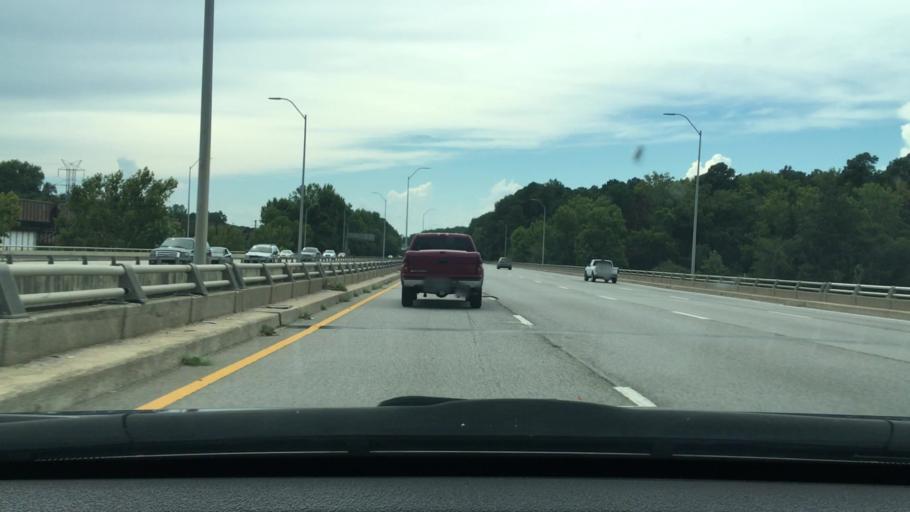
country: US
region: South Carolina
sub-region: Lexington County
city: West Columbia
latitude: 34.0094
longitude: -81.0597
